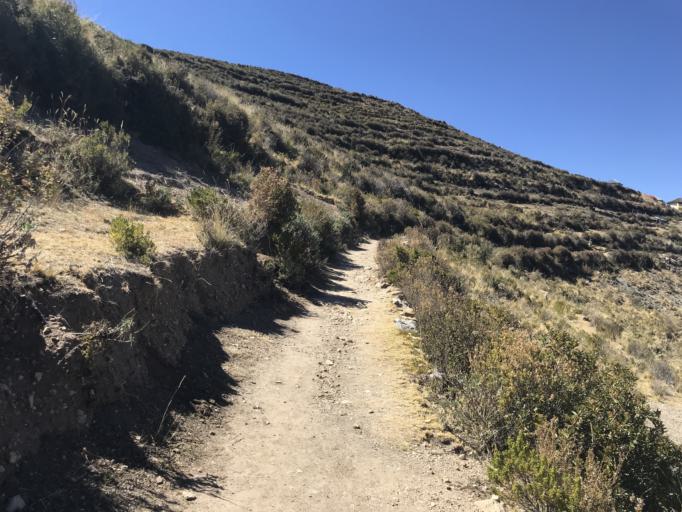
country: BO
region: La Paz
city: Yumani
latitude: -16.0313
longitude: -69.1570
